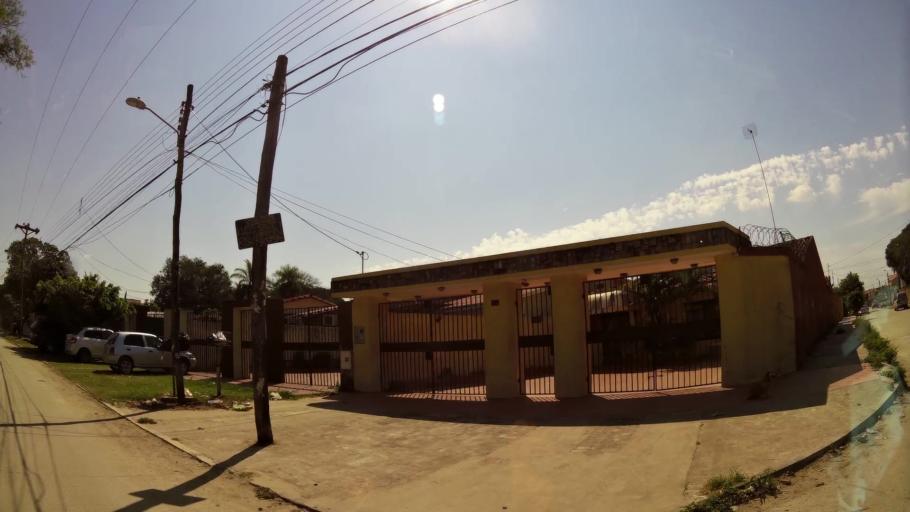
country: BO
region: Santa Cruz
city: Santa Cruz de la Sierra
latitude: -17.7321
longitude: -63.1572
